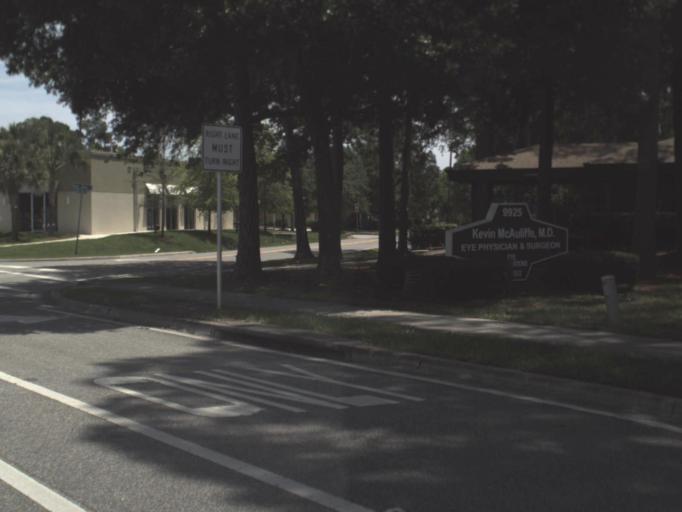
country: US
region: Florida
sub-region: Saint Johns County
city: Fruit Cove
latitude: 30.1972
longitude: -81.6214
